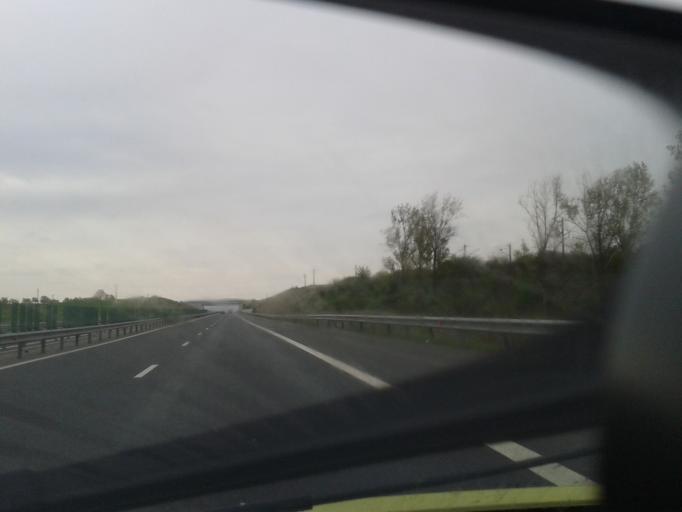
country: RO
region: Hunedoara
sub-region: Comuna Turdas
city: Turdas
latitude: 45.8426
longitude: 23.1256
